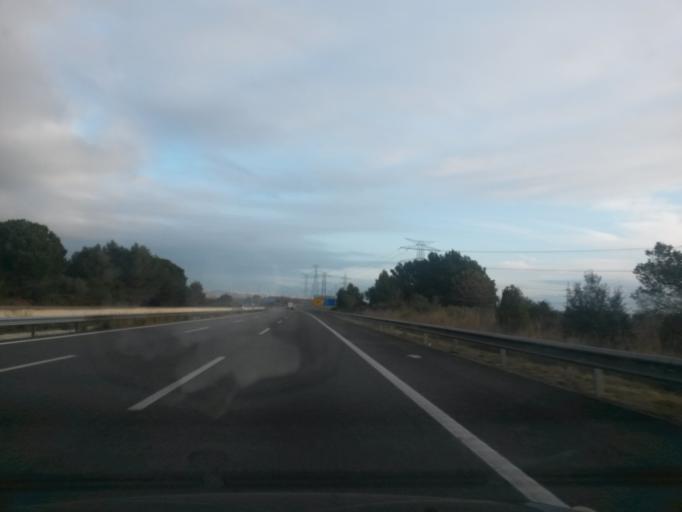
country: ES
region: Catalonia
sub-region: Provincia de Girona
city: Garrigas
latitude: 42.2054
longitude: 2.9376
